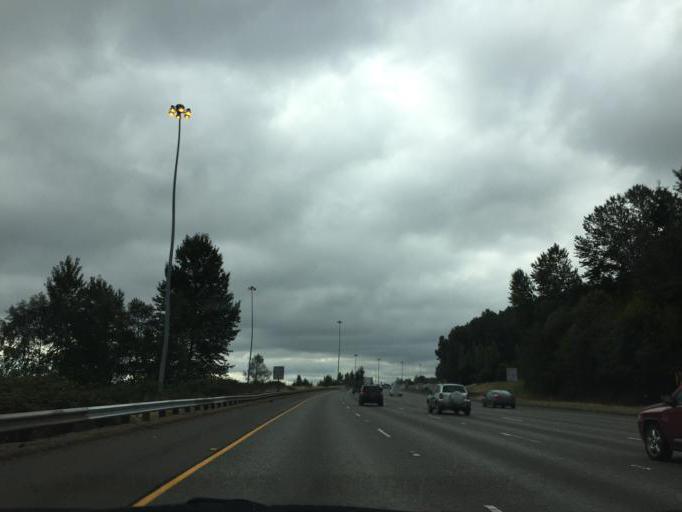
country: US
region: Washington
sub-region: King County
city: Tukwila
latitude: 47.4610
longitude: -122.2649
